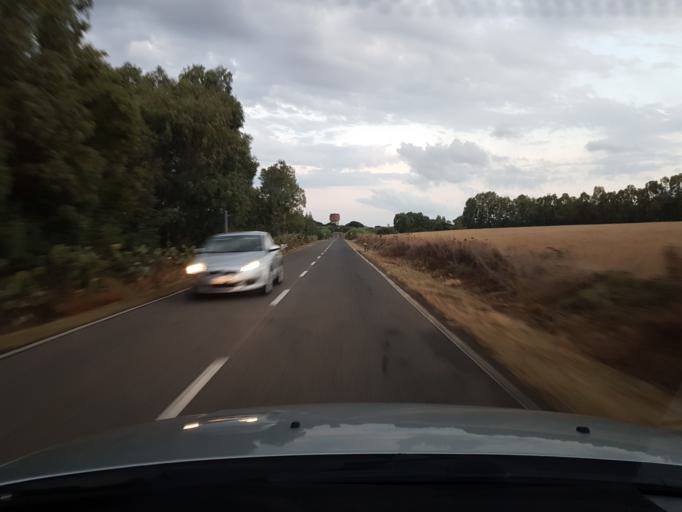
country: IT
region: Sardinia
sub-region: Provincia di Oristano
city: Tramatza
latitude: 40.0119
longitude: 8.6454
